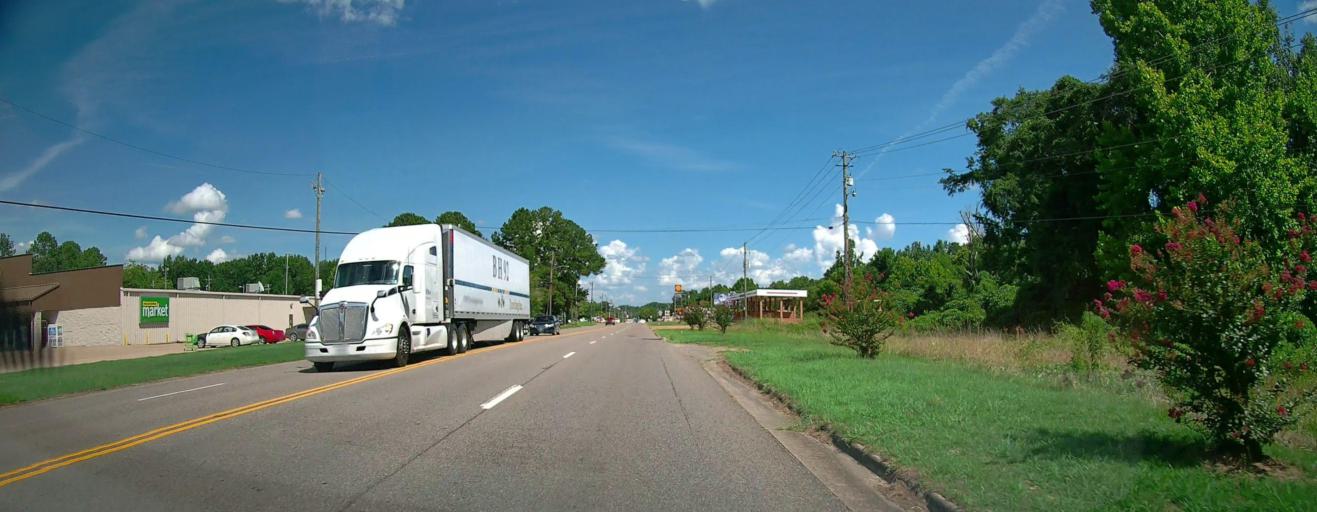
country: US
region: Alabama
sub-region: Pickens County
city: Reform
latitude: 33.3829
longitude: -88.0242
